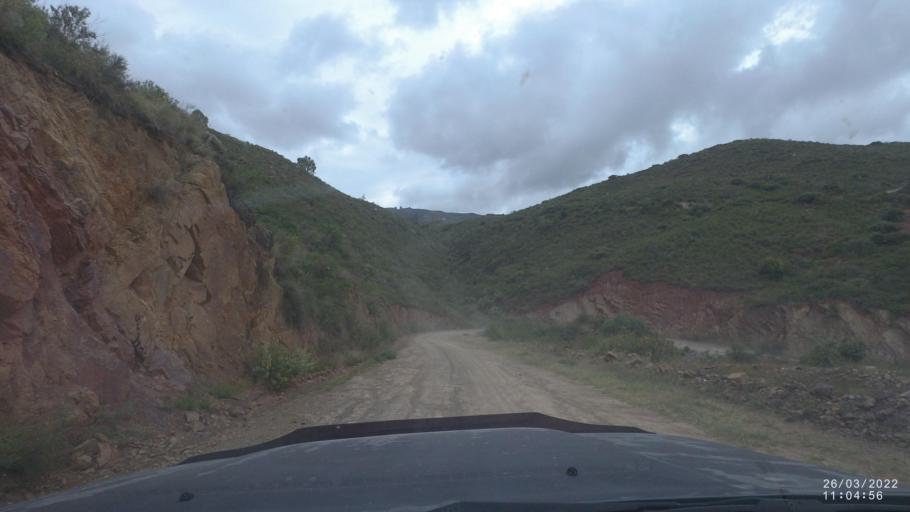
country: BO
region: Cochabamba
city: Tarata
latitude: -17.5306
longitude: -66.0246
